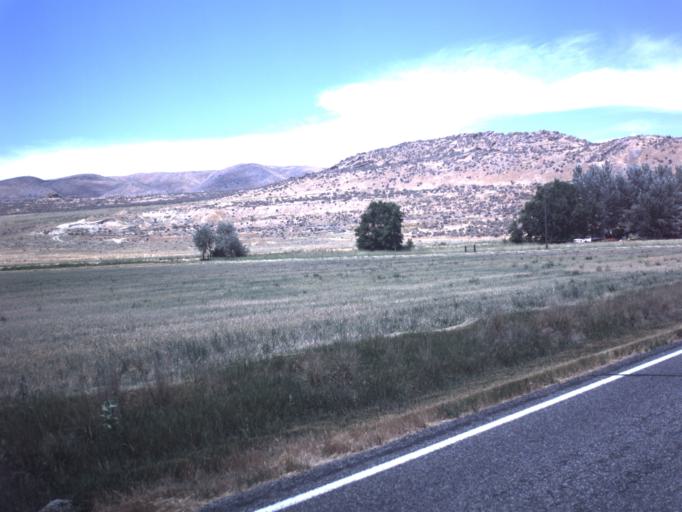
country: US
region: Utah
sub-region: Box Elder County
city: Tremonton
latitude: 41.6323
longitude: -112.3308
